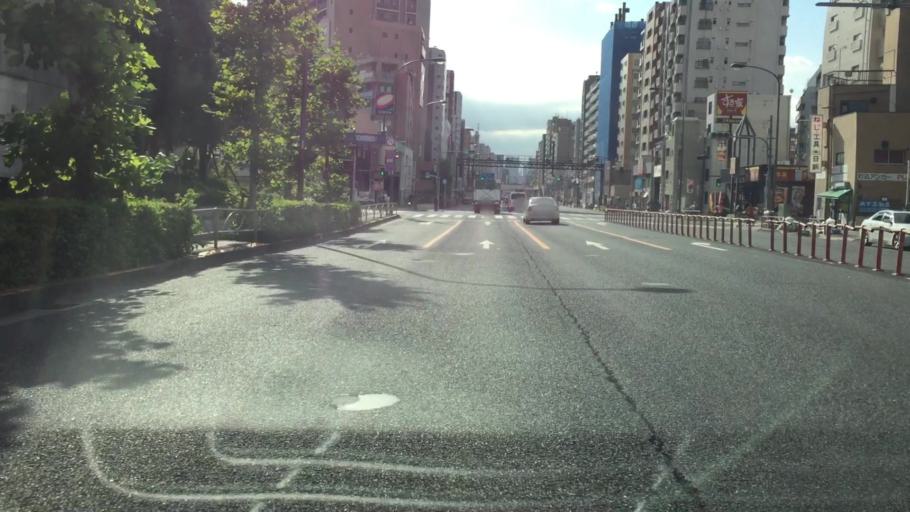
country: JP
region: Saitama
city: Soka
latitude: 35.7273
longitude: 139.7896
